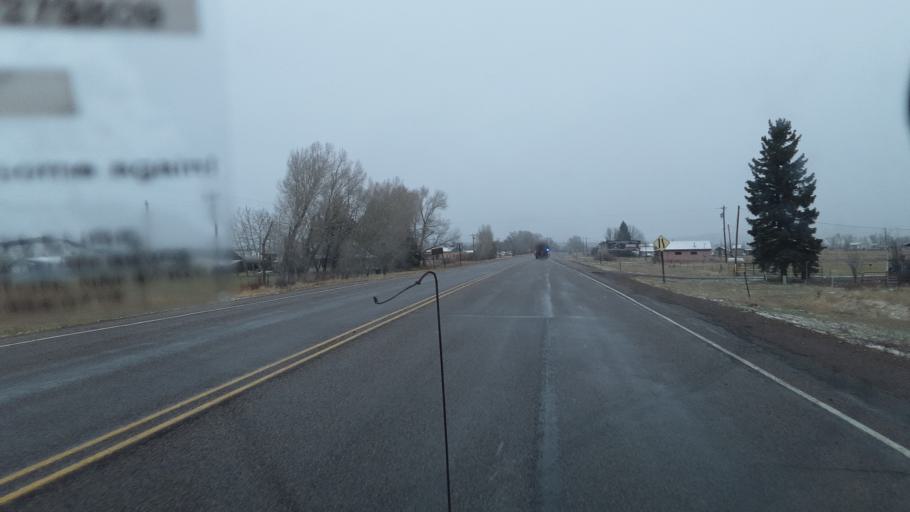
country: US
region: New Mexico
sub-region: Rio Arriba County
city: Tierra Amarilla
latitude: 36.7384
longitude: -106.5685
